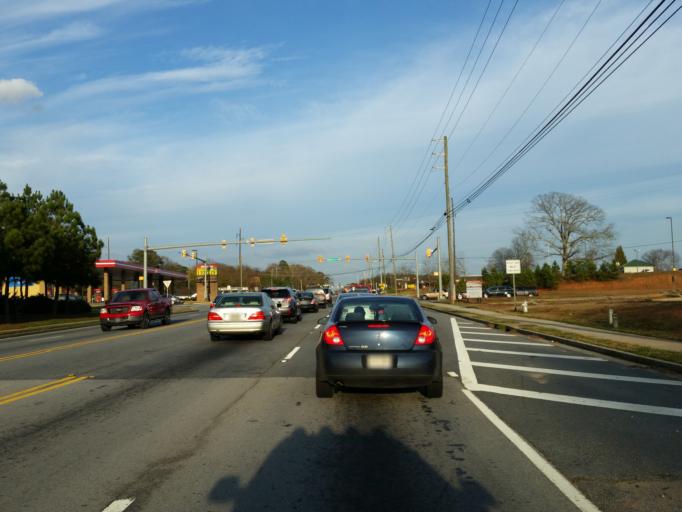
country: US
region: Georgia
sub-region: Cobb County
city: Powder Springs
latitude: 33.8657
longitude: -84.6344
